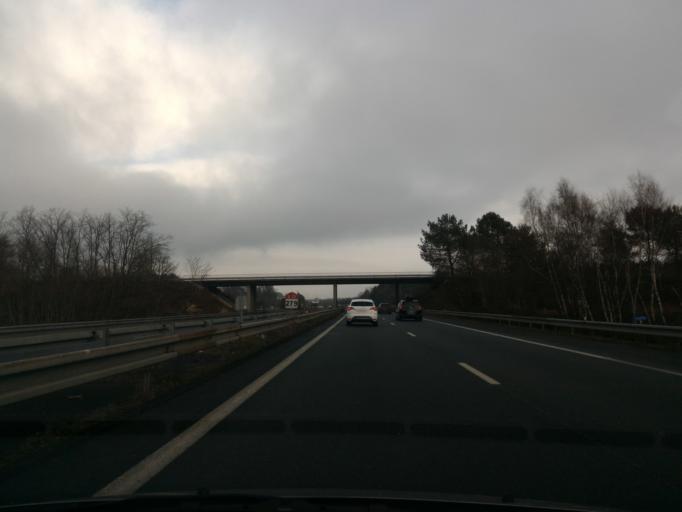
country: FR
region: Poitou-Charentes
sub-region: Departement de la Vienne
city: Naintre
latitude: 46.7801
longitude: 0.4991
